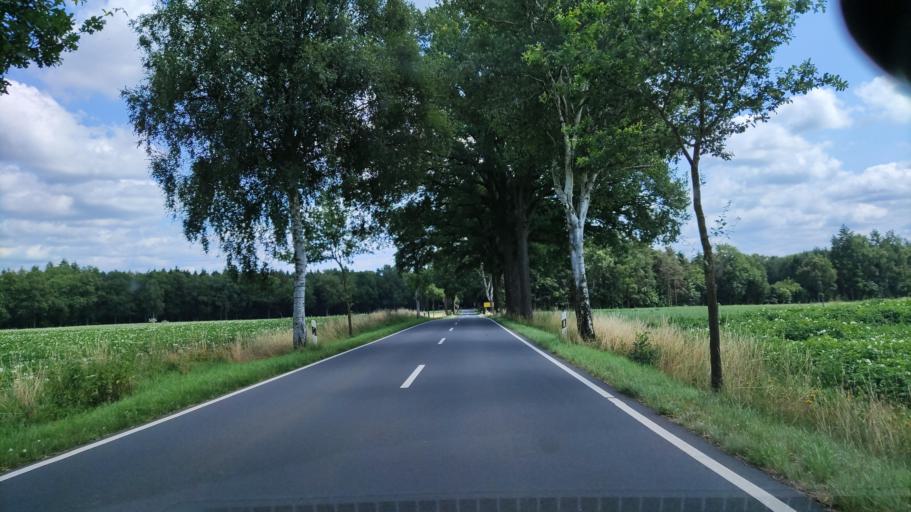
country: DE
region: Lower Saxony
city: Walsrode
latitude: 52.9127
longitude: 9.5695
